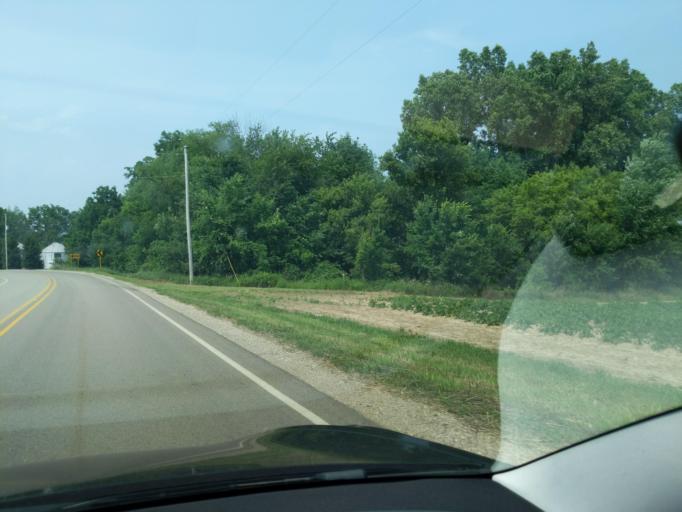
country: US
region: Michigan
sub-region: Clinton County
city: DeWitt
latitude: 42.8938
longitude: -84.5724
